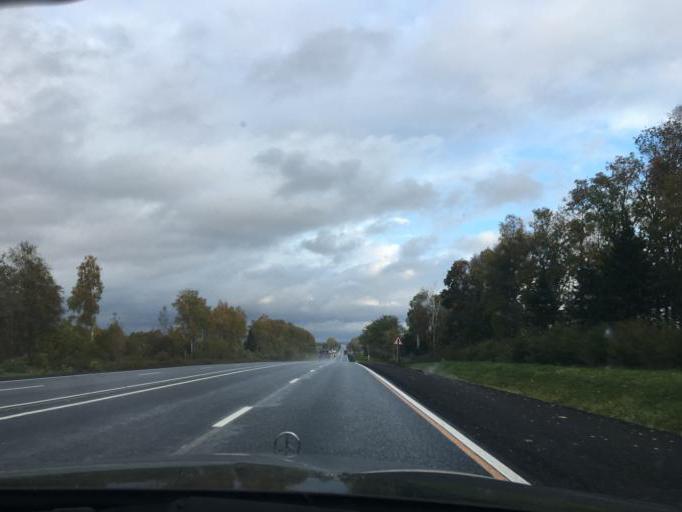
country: RU
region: Smolensk
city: Katyn'
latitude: 54.8484
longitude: 31.7850
